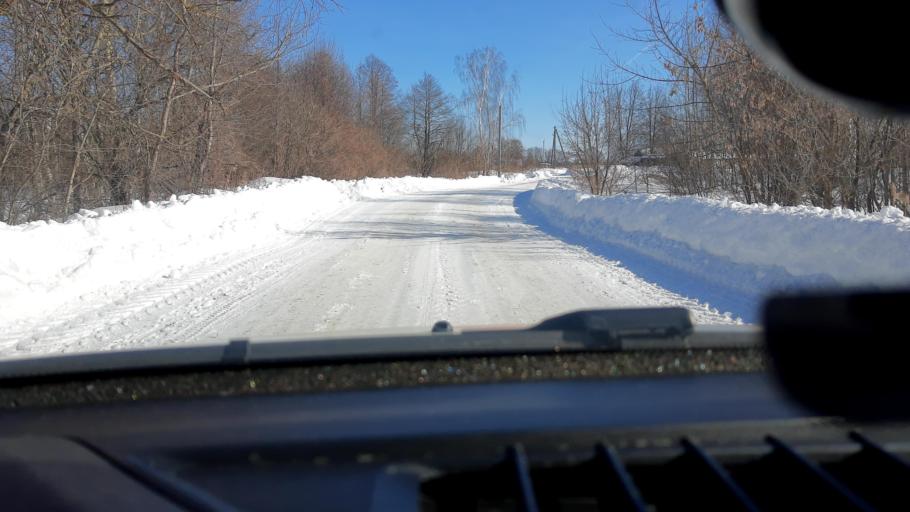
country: RU
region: Nizjnij Novgorod
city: Volodarsk
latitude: 56.2464
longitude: 43.1835
